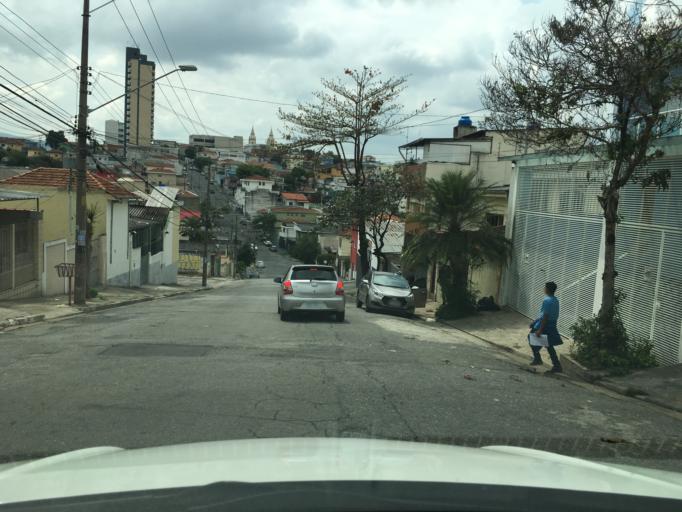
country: BR
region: Sao Paulo
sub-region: Sao Paulo
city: Sao Paulo
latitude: -23.4968
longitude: -46.6508
